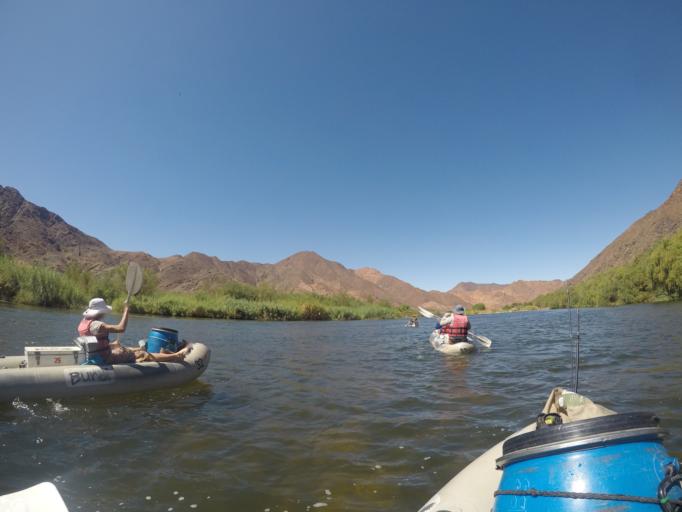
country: ZA
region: Northern Cape
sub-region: Namakwa District Municipality
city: Port Nolloth
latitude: -28.7166
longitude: 17.4380
